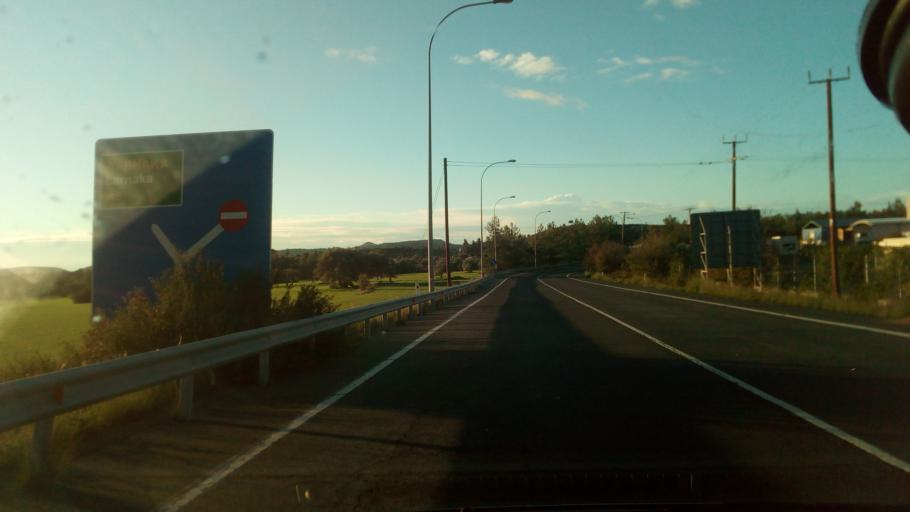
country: CY
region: Larnaka
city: Kofinou
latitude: 34.8353
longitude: 33.3996
